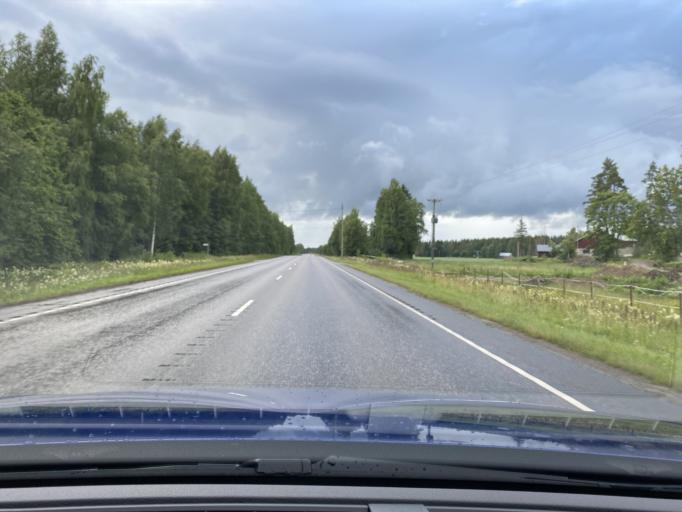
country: FI
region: Uusimaa
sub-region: Helsinki
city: Nurmijaervi
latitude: 60.5456
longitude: 24.8306
